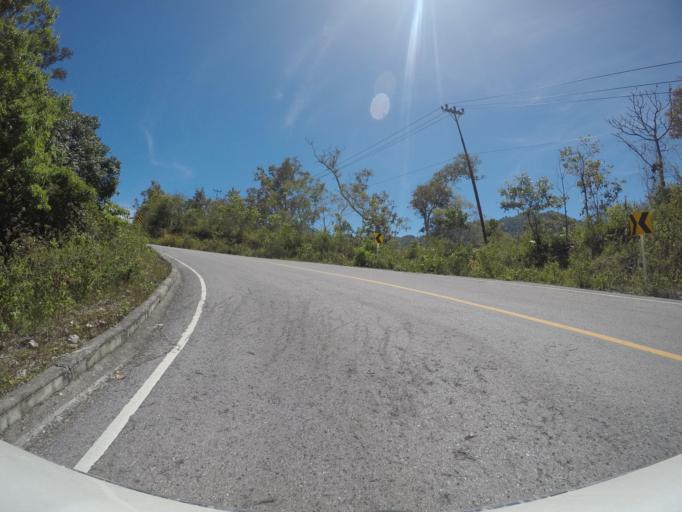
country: TL
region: Manatuto
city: Manatuto
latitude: -8.8160
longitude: 125.9736
